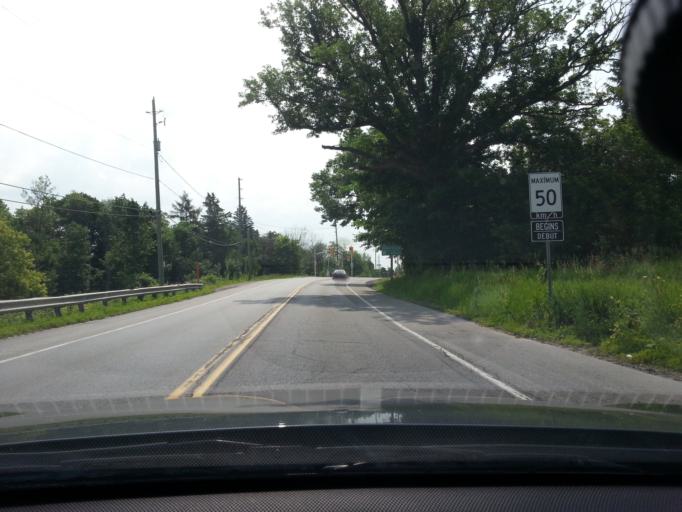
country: CA
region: Ontario
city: Bells Corners
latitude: 45.2294
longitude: -75.6910
